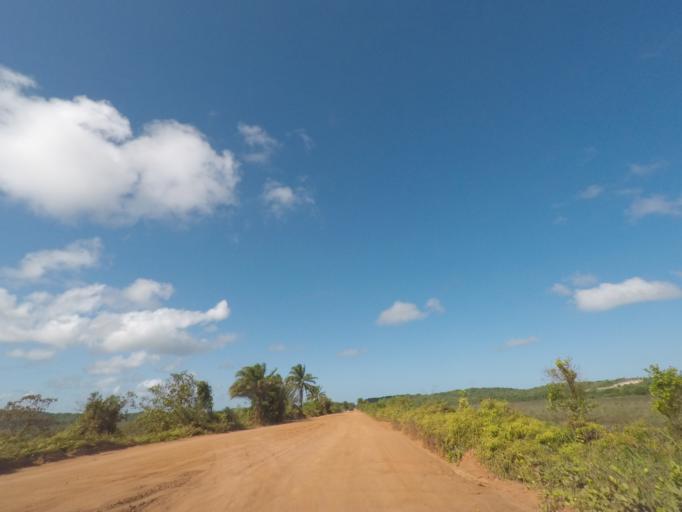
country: BR
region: Bahia
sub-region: Marau
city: Marau
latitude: -14.1468
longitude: -39.0039
